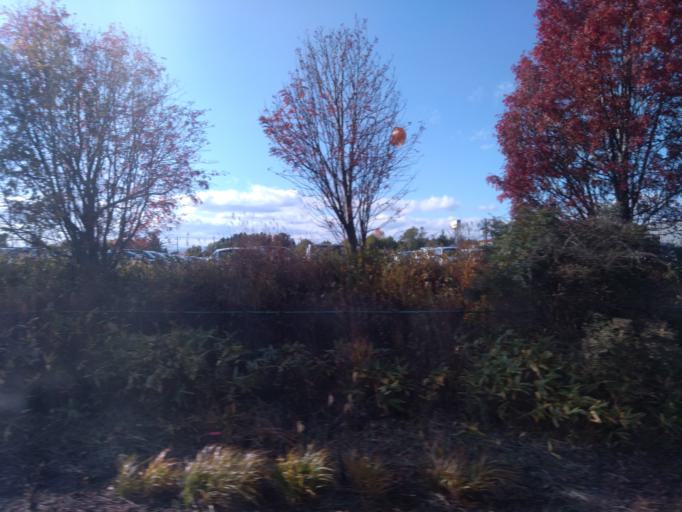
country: JP
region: Hokkaido
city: Kitahiroshima
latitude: 42.9259
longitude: 141.5729
